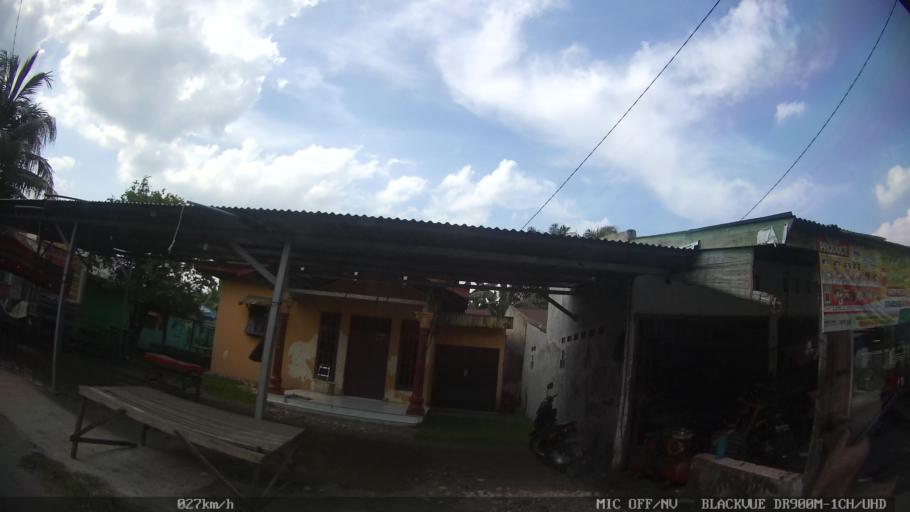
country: ID
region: North Sumatra
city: Binjai
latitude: 3.6132
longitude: 98.5187
